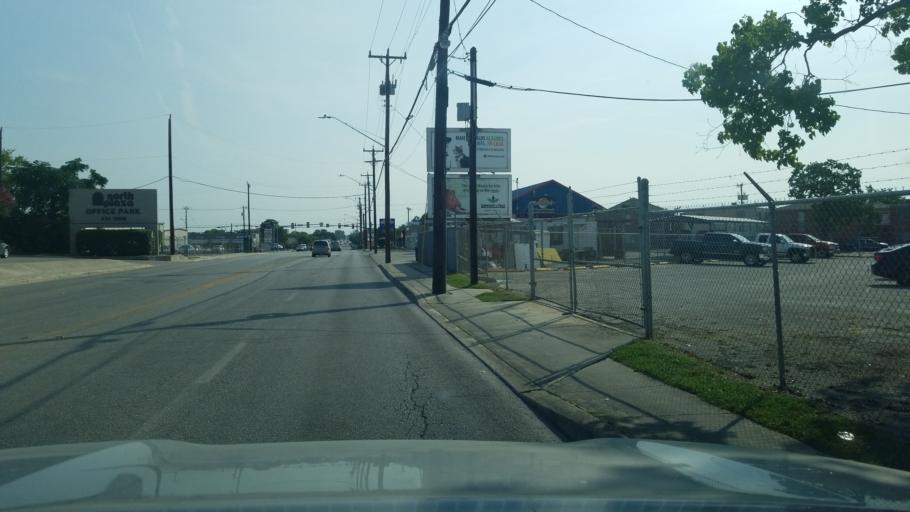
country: US
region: Texas
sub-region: Bexar County
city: Castle Hills
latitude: 29.5273
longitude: -98.4941
